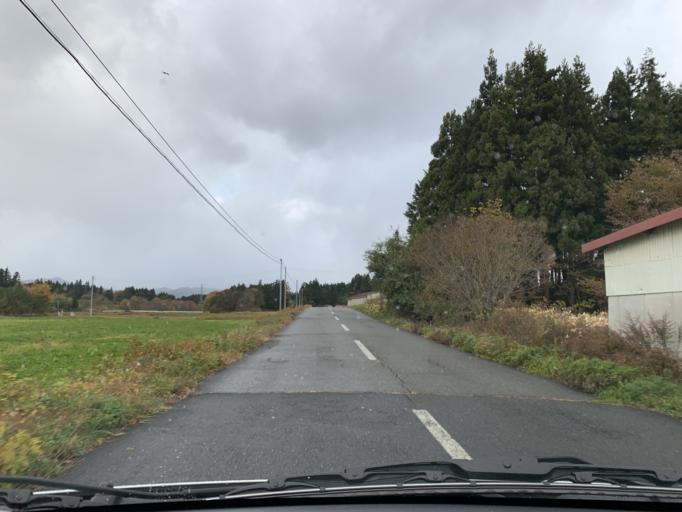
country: JP
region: Iwate
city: Mizusawa
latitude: 39.0913
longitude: 140.9974
